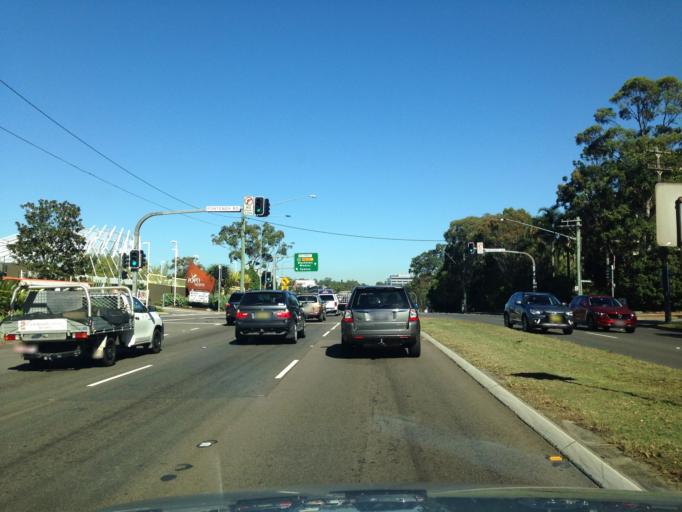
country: AU
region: New South Wales
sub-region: Ryde
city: North Ryde
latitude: -33.7795
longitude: 151.1344
